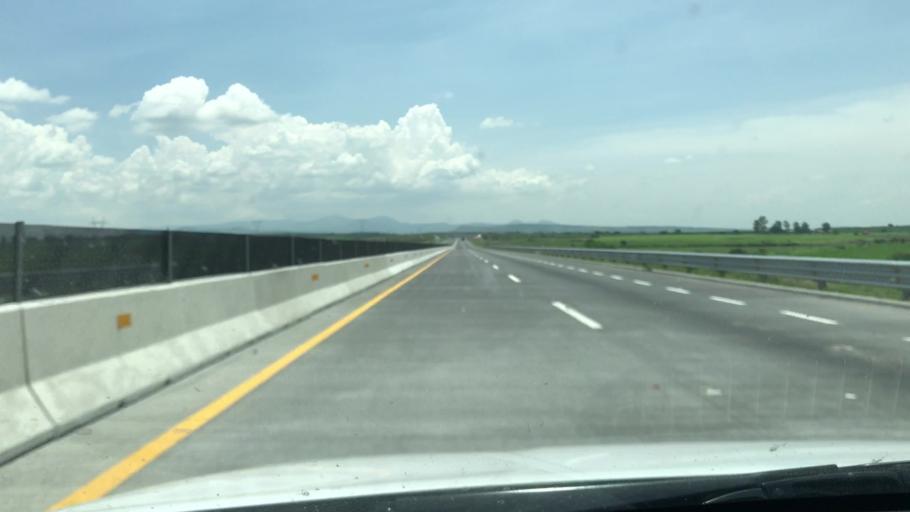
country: MX
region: Michoacan
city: La Piedad Cavadas
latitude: 20.4003
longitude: -102.0479
